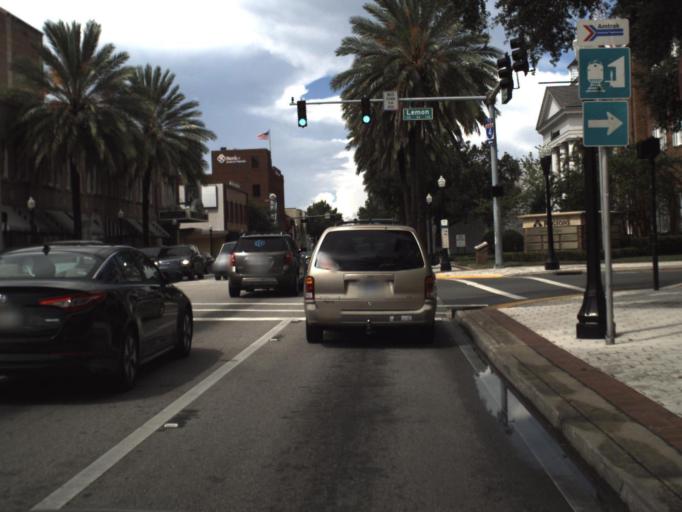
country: US
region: Florida
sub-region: Polk County
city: Lakeland
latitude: 28.0426
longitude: -81.9571
